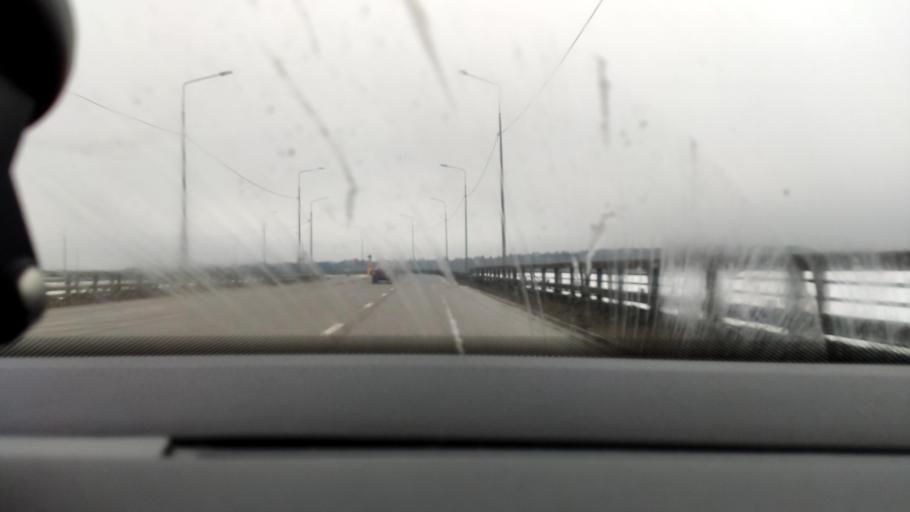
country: RU
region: Moskovskaya
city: Sergiyev Posad
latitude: 56.2747
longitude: 38.1180
